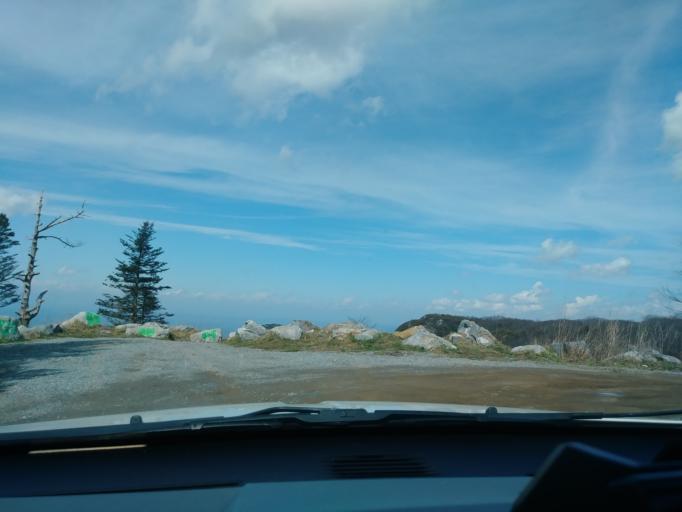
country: US
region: Tennessee
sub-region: Greene County
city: Tusculum
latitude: 36.0316
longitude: -82.7052
